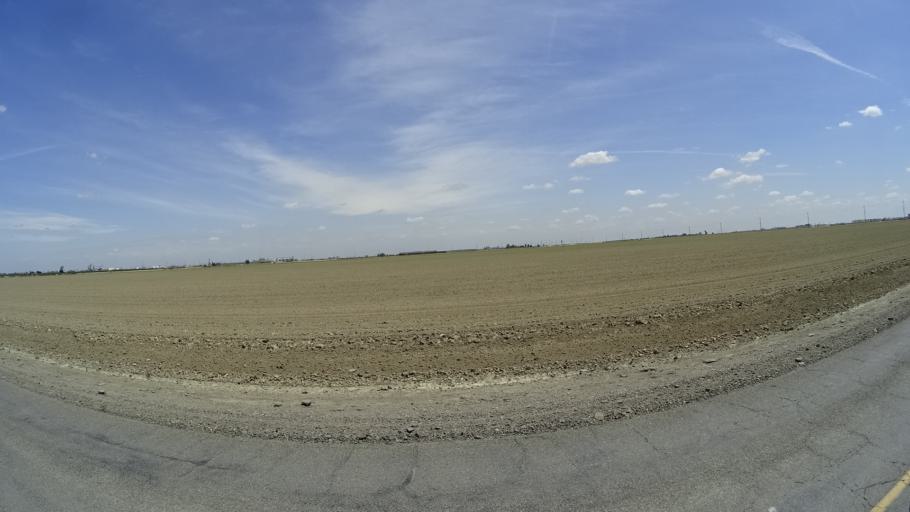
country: US
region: California
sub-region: Kings County
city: Home Garden
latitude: 36.2585
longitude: -119.6728
